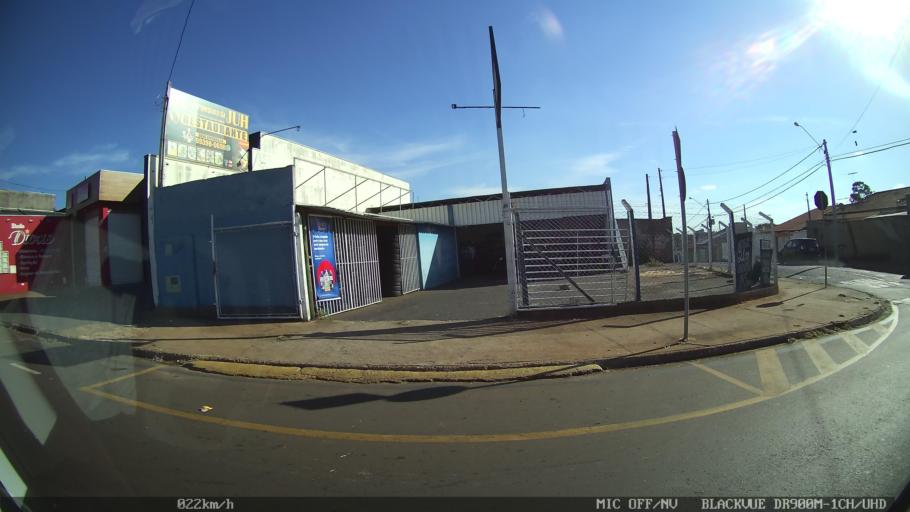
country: BR
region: Sao Paulo
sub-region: Franca
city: Franca
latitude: -20.5198
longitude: -47.4368
